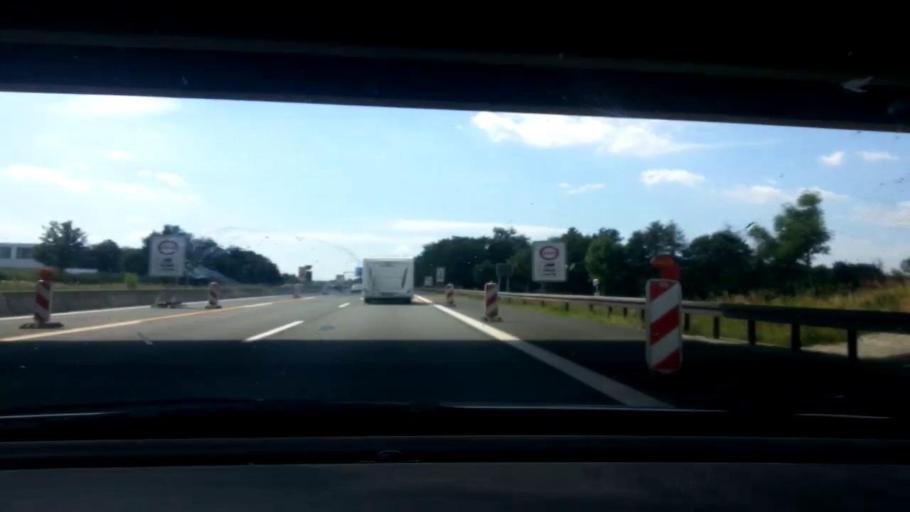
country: DE
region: Bavaria
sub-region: Upper Franconia
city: Bindlach
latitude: 49.9689
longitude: 11.6054
